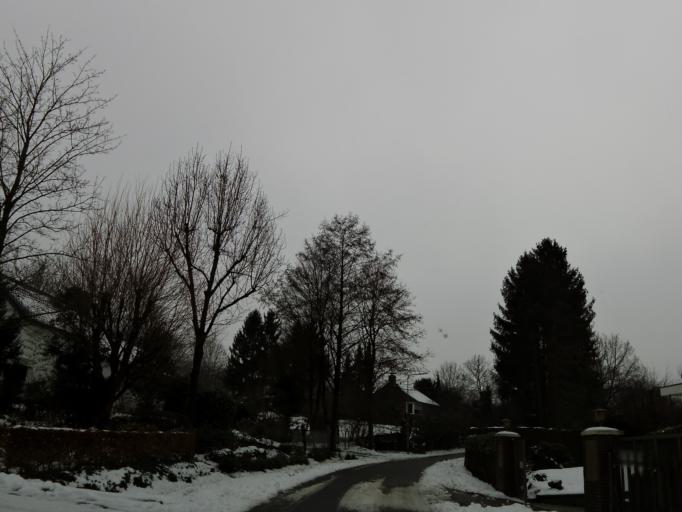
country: NL
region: Limburg
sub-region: Gemeente Vaals
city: Vaals
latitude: 50.7656
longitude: 5.9897
